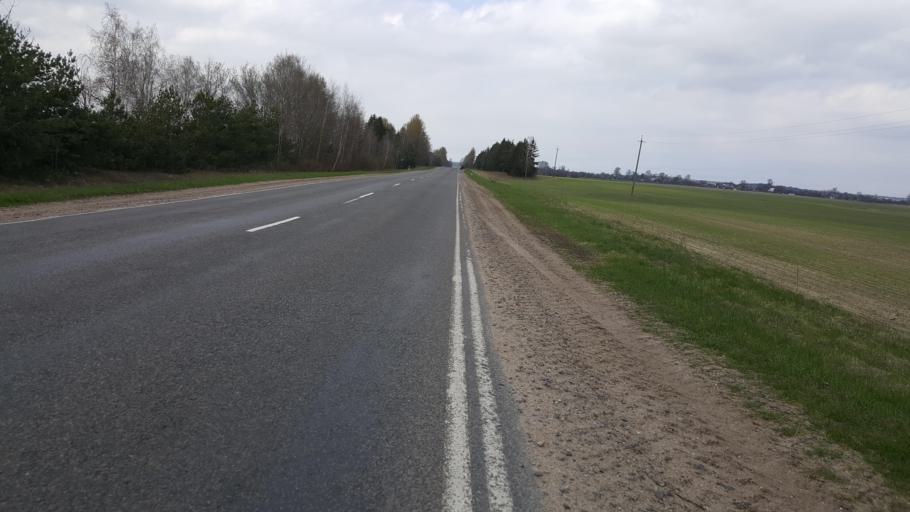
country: BY
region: Brest
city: Kamyanyets
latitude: 52.3482
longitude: 23.9017
